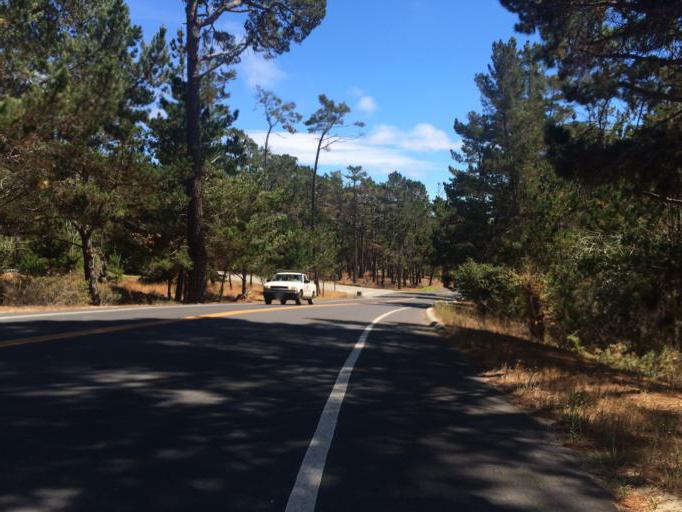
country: US
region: California
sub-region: Monterey County
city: Del Monte Forest
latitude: 36.5800
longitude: -121.9568
